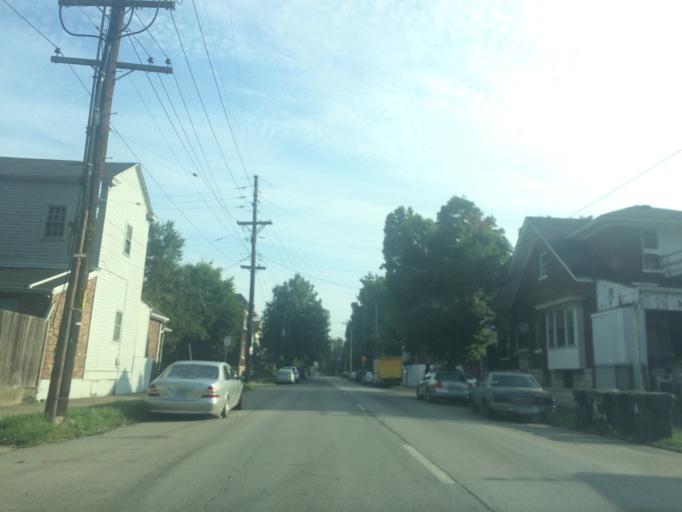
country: US
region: Kentucky
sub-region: Jefferson County
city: Louisville
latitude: 38.2313
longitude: -85.7481
